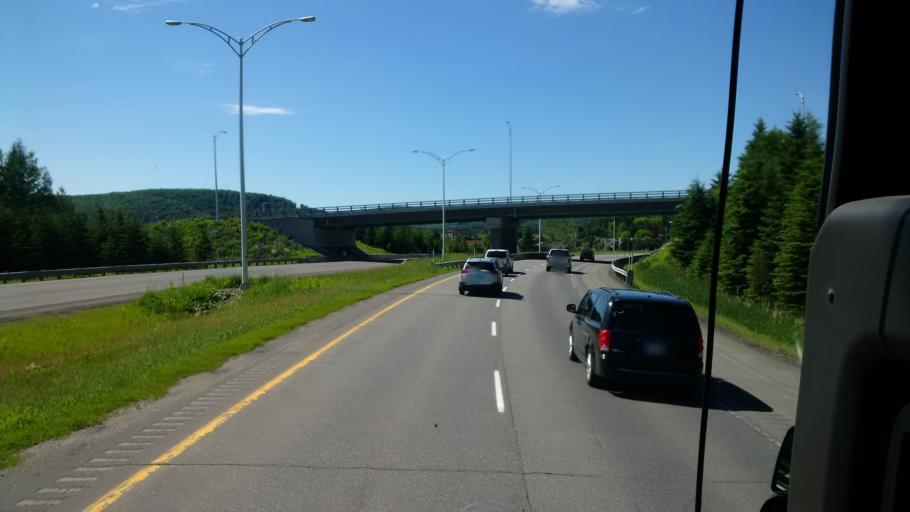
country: CA
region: Quebec
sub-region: Laurentides
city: Saint-Sauveur
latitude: 45.8909
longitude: -74.1455
